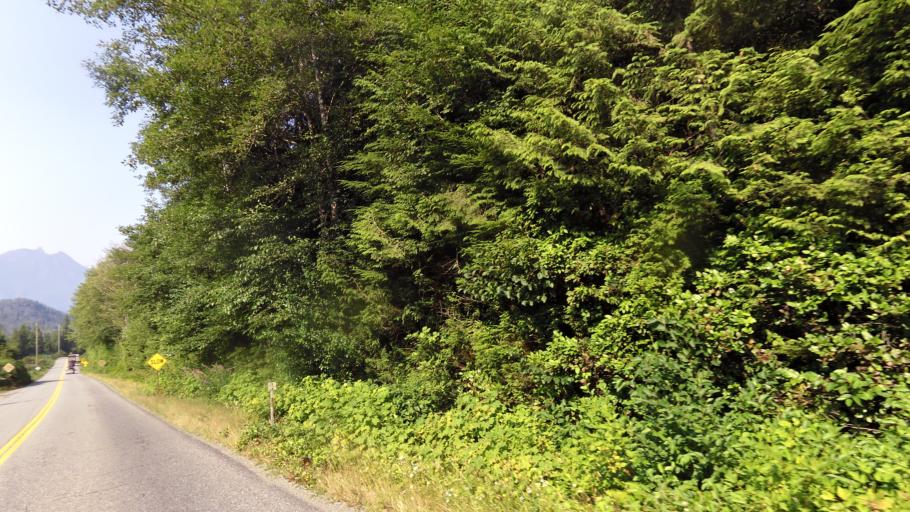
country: CA
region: British Columbia
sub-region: Regional District of Alberni-Clayoquot
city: Ucluelet
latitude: 49.0796
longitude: -125.4650
